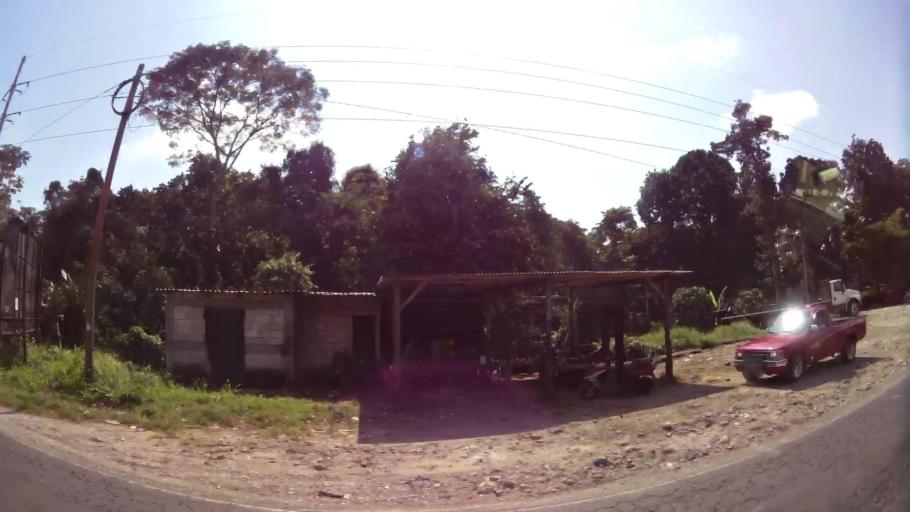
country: GT
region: Suchitepeque
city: Mazatenango
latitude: 14.5522
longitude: -91.5089
